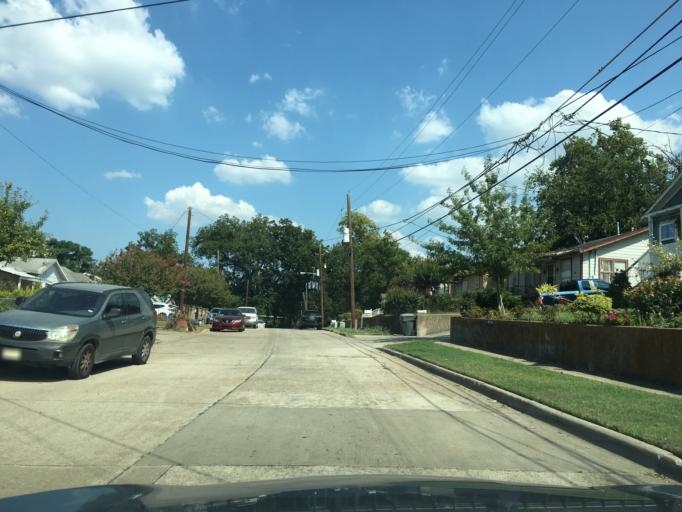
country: US
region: Texas
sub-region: Dallas County
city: Dallas
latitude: 32.7483
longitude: -96.7946
